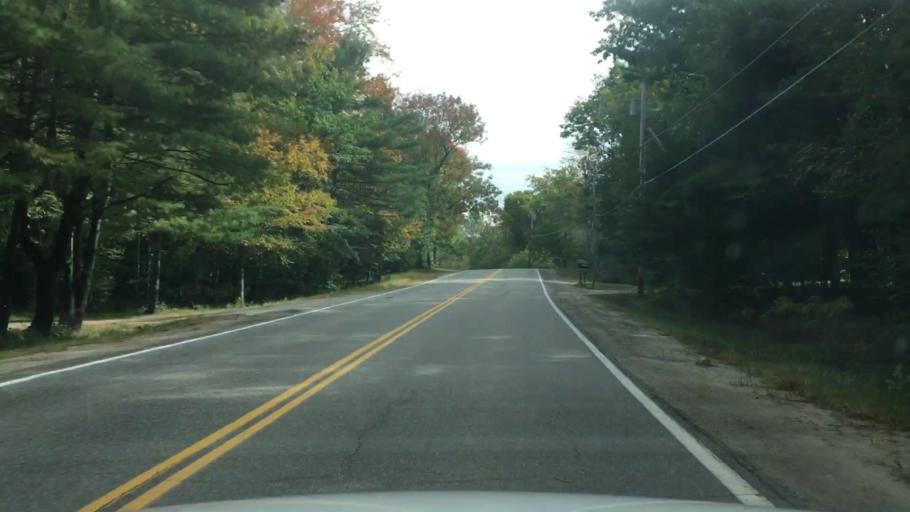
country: US
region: Maine
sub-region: Sagadahoc County
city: Topsham
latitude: 43.9362
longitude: -70.0188
